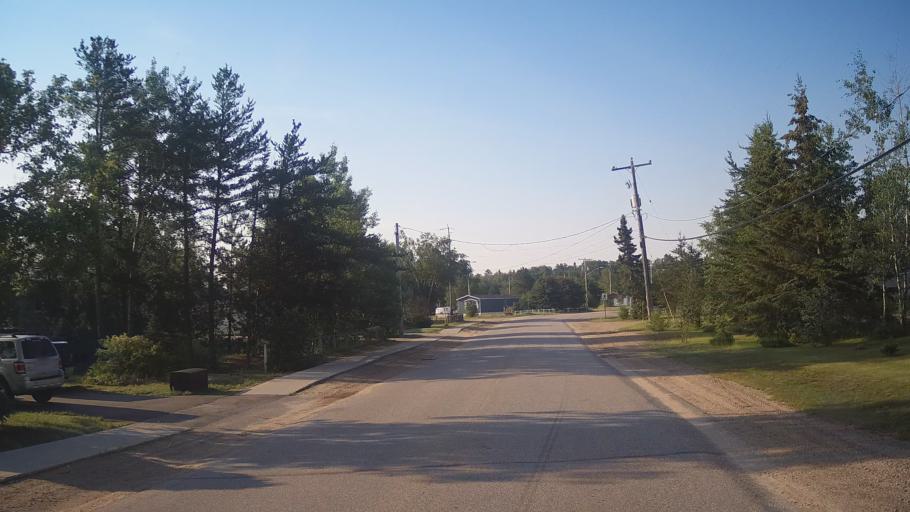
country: CA
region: Ontario
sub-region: Rainy River District
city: Atikokan
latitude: 49.4077
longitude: -91.6576
